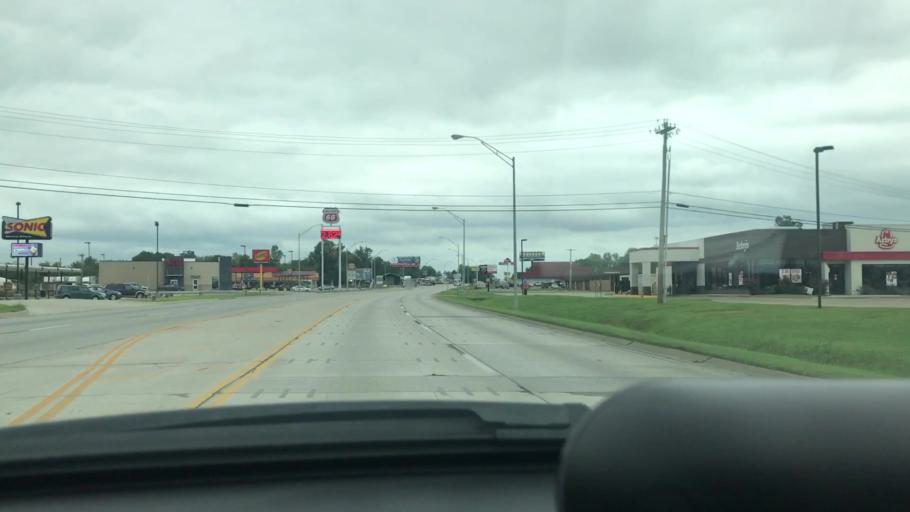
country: US
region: Oklahoma
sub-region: Wagoner County
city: Wagoner
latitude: 35.9600
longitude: -95.3946
